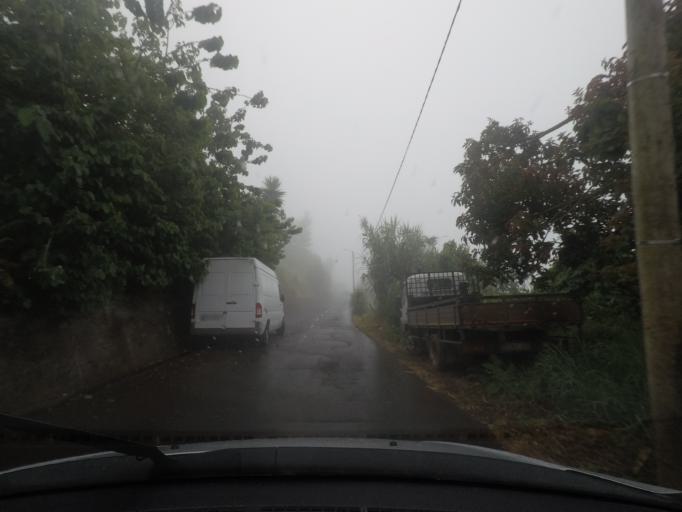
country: PT
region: Madeira
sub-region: Santana
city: Santana
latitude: 32.7722
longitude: -16.8758
